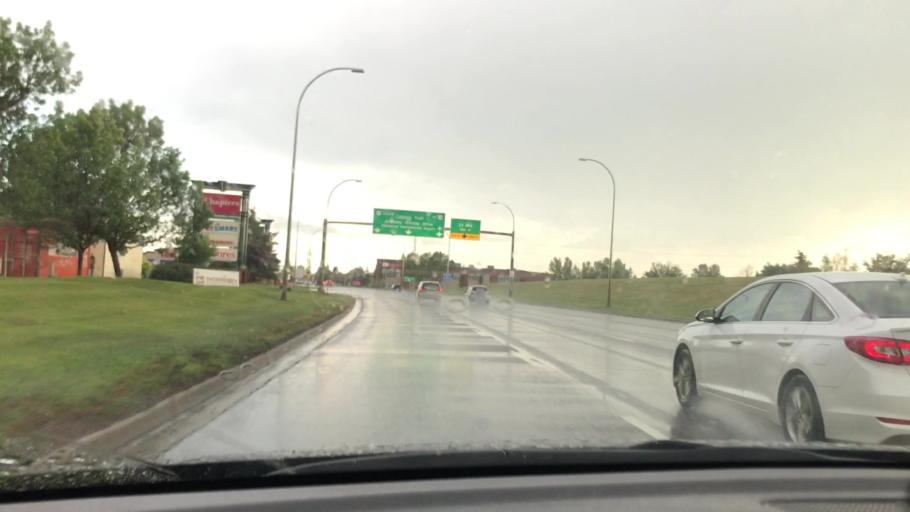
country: CA
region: Alberta
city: Edmonton
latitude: 53.4660
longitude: -113.4956
